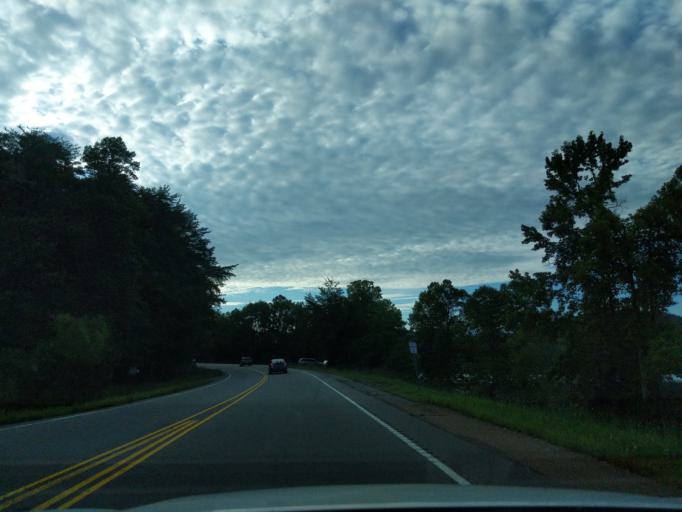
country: US
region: Tennessee
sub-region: Polk County
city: Benton
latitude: 35.1123
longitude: -84.5869
